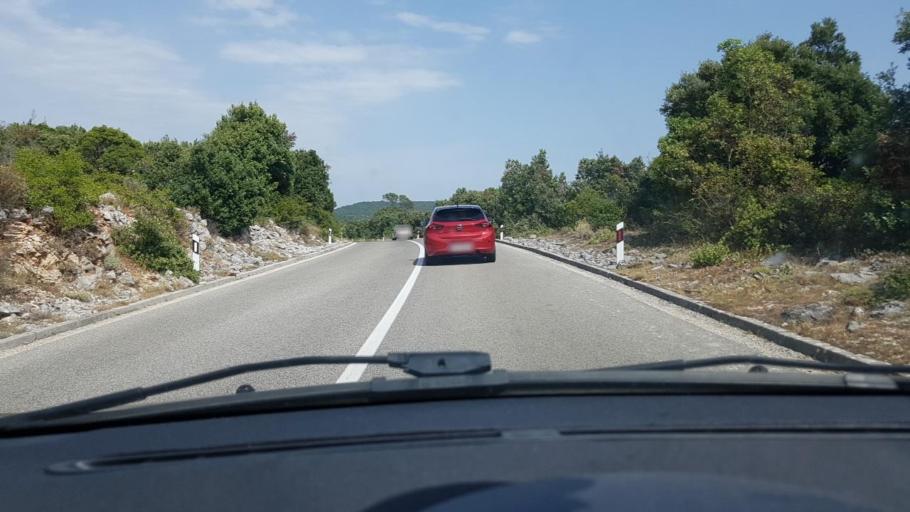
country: HR
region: Dubrovacko-Neretvanska
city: Smokvica
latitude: 42.9484
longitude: 16.9789
